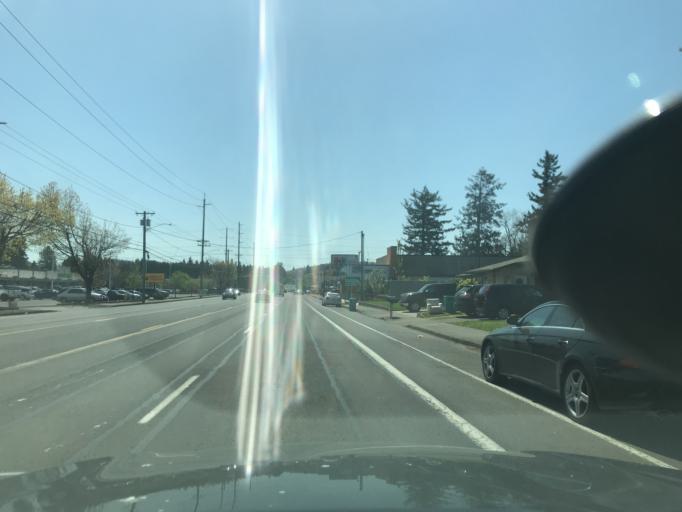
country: US
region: Oregon
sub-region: Multnomah County
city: Gresham
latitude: 45.5065
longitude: -122.4758
